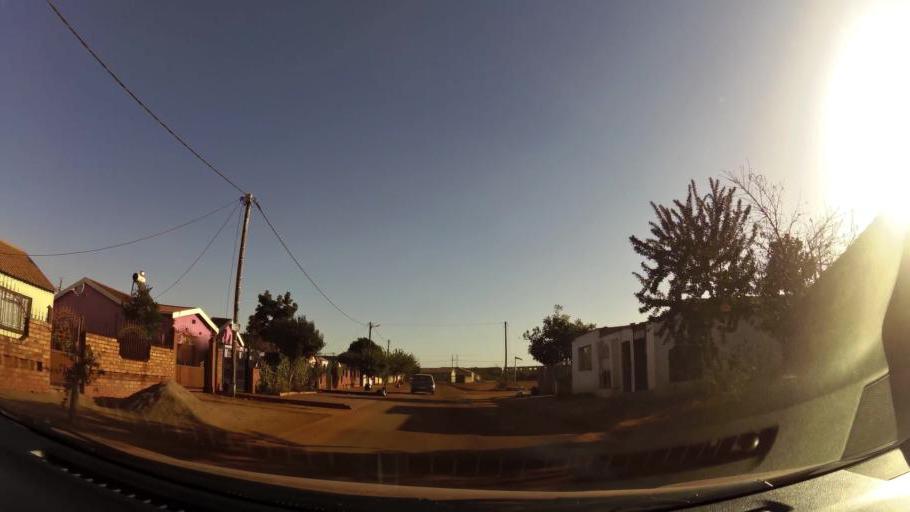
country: ZA
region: Gauteng
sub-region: City of Tshwane Metropolitan Municipality
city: Mabopane
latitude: -25.5914
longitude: 28.0965
